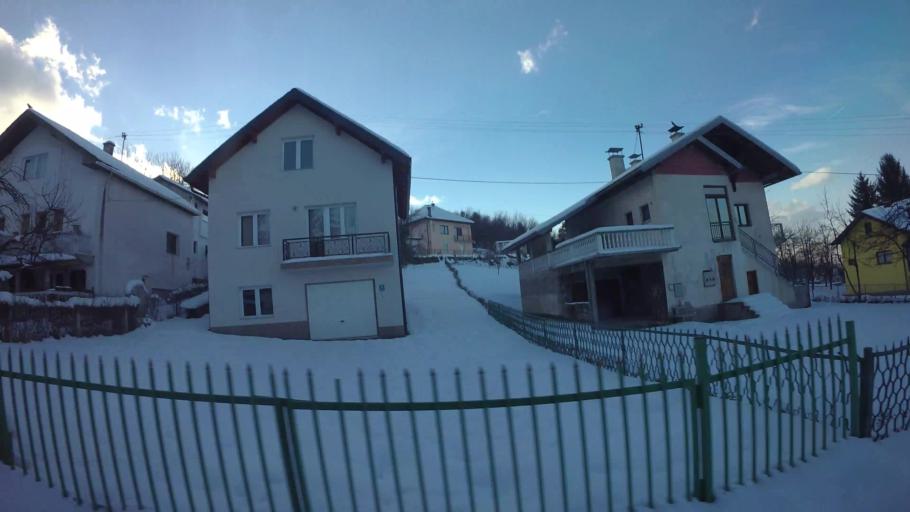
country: BA
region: Federation of Bosnia and Herzegovina
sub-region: Kanton Sarajevo
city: Sarajevo
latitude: 43.8066
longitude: 18.3581
